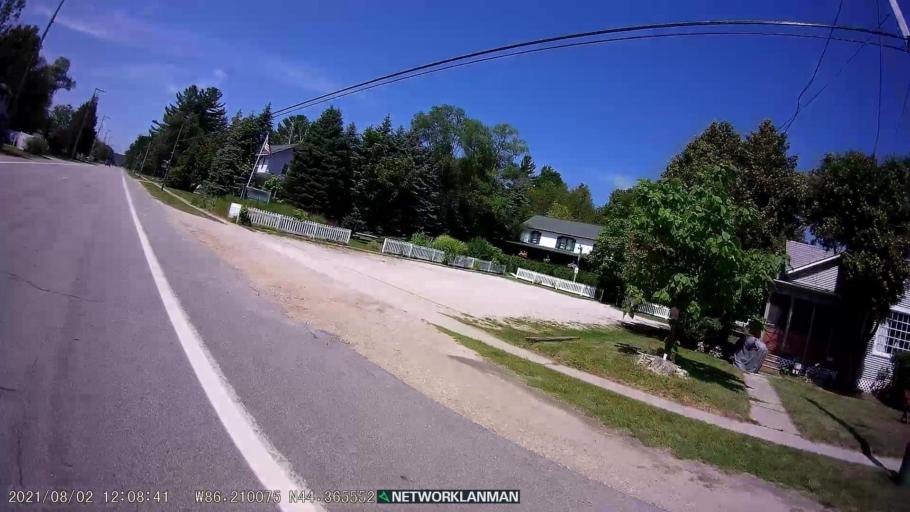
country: US
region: Michigan
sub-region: Manistee County
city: Manistee
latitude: 44.3657
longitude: -86.2101
